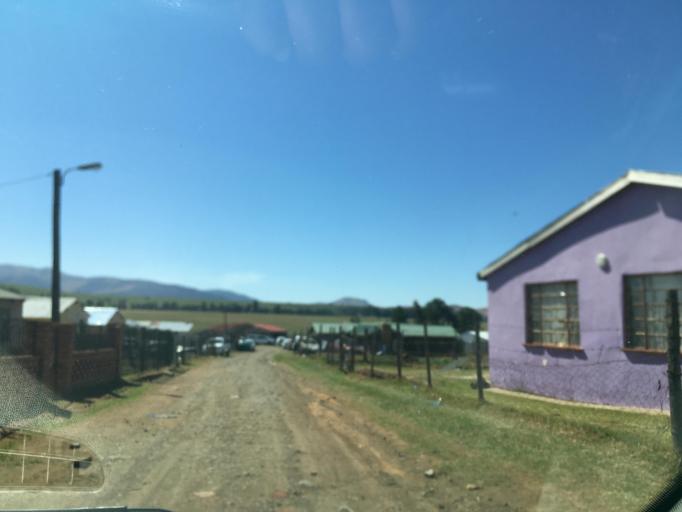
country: ZA
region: Eastern Cape
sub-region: Chris Hani District Municipality
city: Elliot
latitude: -31.3282
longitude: 27.8256
